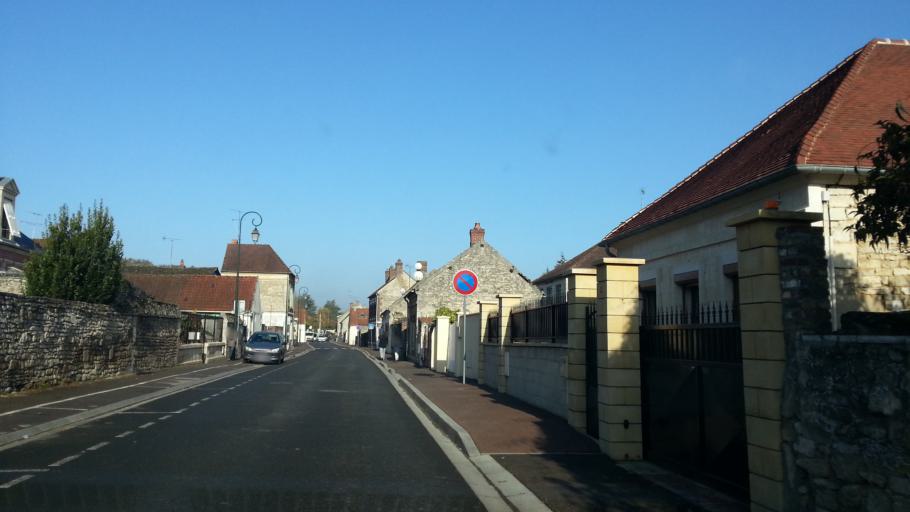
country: FR
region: Picardie
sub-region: Departement de l'Oise
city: Balagny-sur-Therain
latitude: 49.2986
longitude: 2.3336
